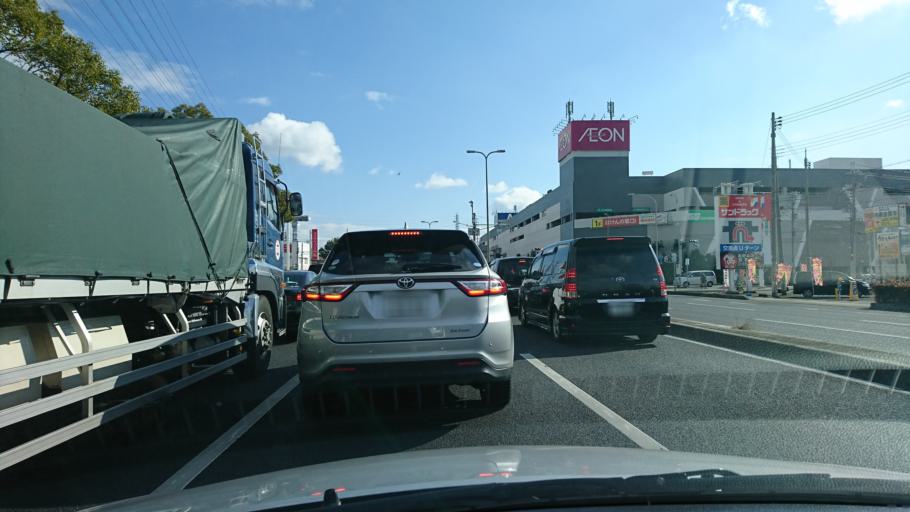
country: JP
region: Hyogo
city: Kakogawacho-honmachi
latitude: 34.7708
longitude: 134.8018
